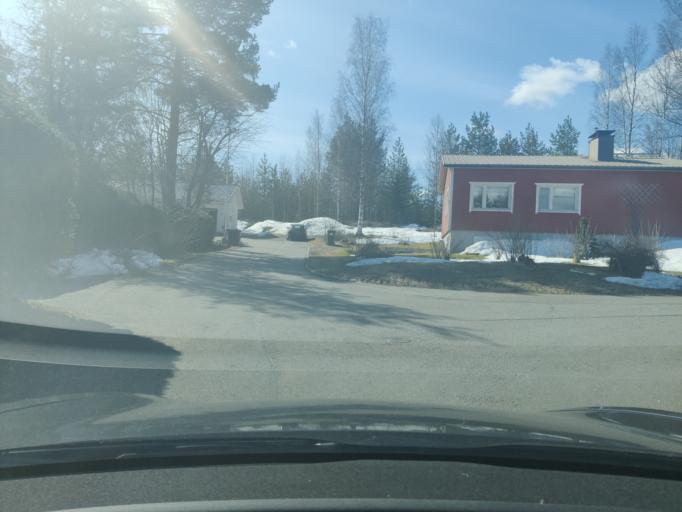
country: FI
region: Northern Savo
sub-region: Kuopio
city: Vehmersalmi
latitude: 62.9129
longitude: 28.1607
